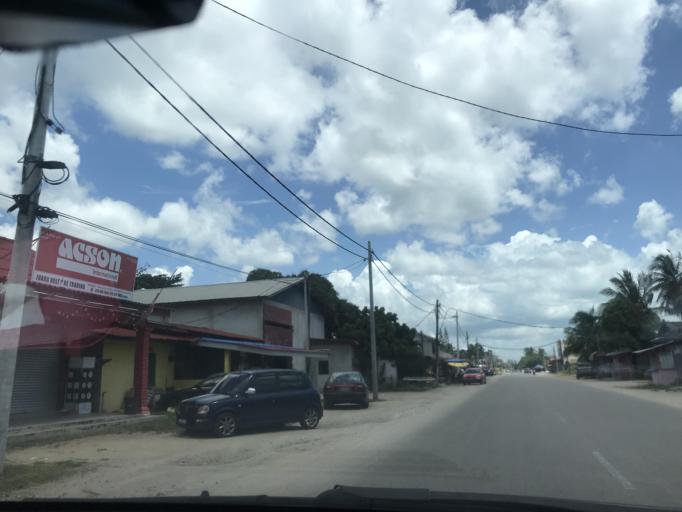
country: TH
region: Narathiwat
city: Tak Bai
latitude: 6.2253
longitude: 102.1038
